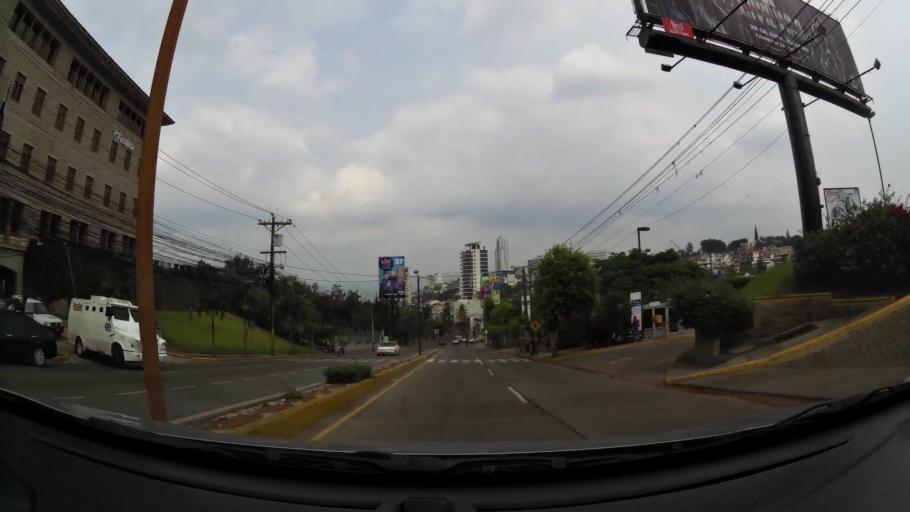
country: HN
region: Francisco Morazan
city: Tegucigalpa
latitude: 14.0891
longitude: -87.1787
